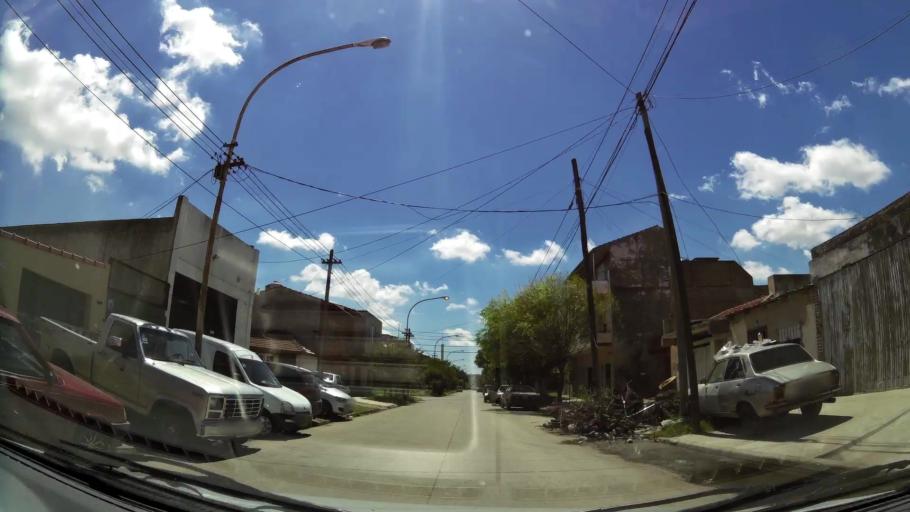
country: AR
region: Buenos Aires
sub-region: Partido de Lanus
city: Lanus
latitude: -34.7029
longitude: -58.4160
